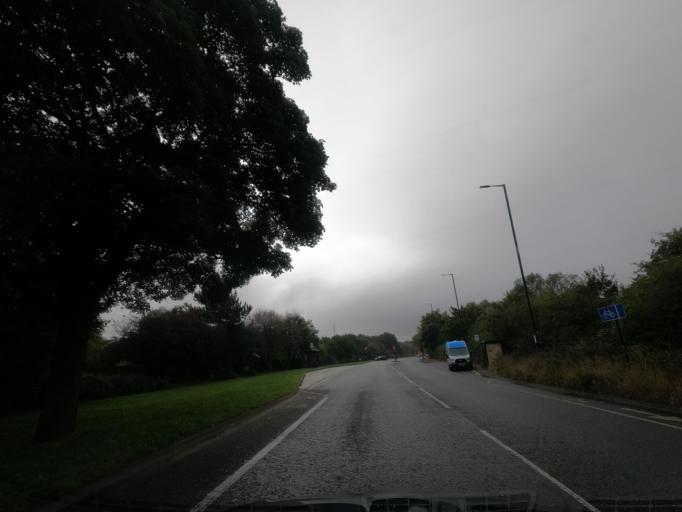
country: GB
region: England
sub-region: Redcar and Cleveland
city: Redcar
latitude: 54.5953
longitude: -1.0825
